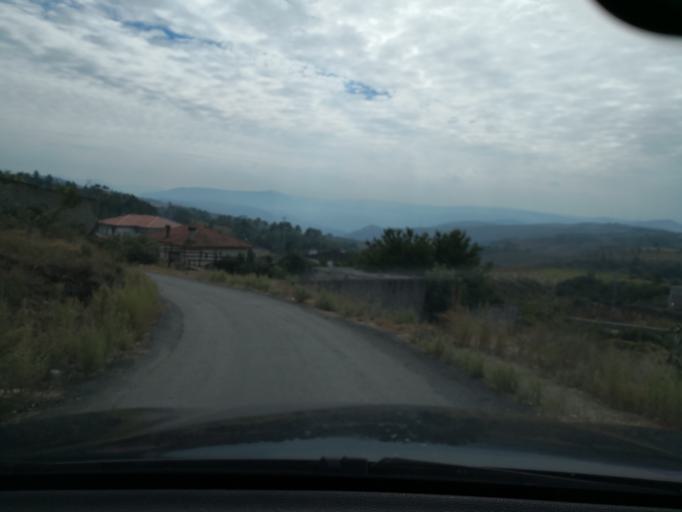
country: PT
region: Vila Real
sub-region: Peso da Regua
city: Peso da Regua
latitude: 41.2034
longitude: -7.7011
